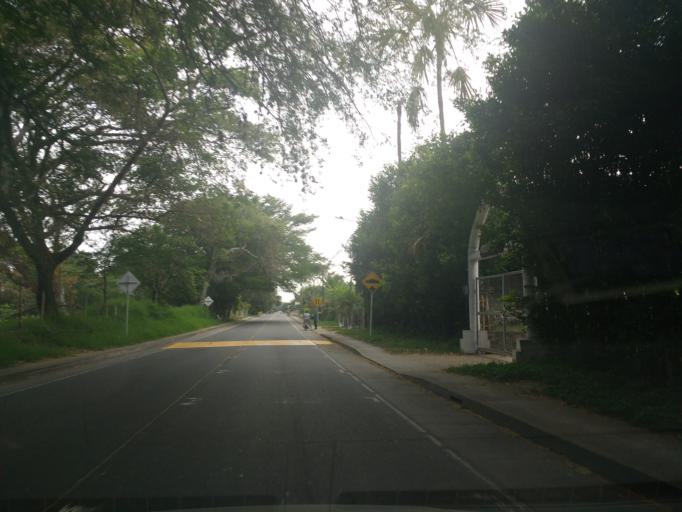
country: CO
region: Cauca
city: Miranda
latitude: 3.2805
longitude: -76.2229
